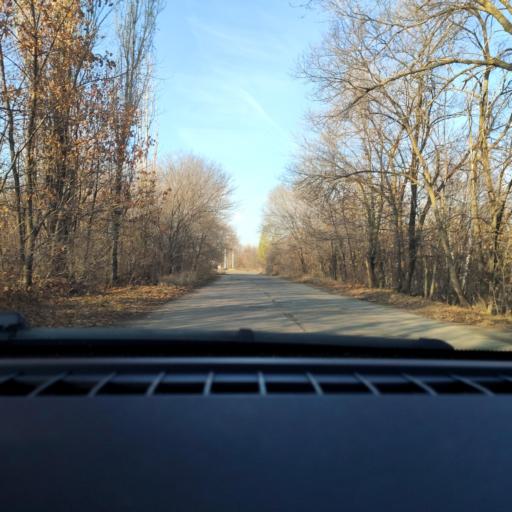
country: RU
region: Voronezj
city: Novaya Usman'
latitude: 51.6389
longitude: 39.3105
